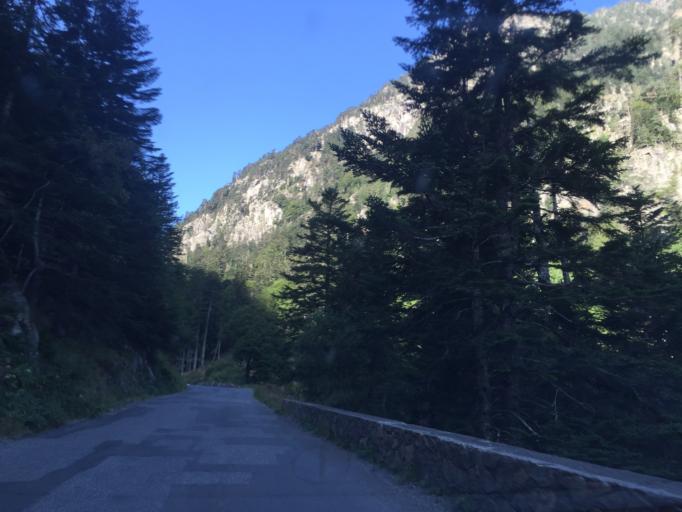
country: FR
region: Midi-Pyrenees
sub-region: Departement des Hautes-Pyrenees
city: Cauterets
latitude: 42.8613
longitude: -0.1219
